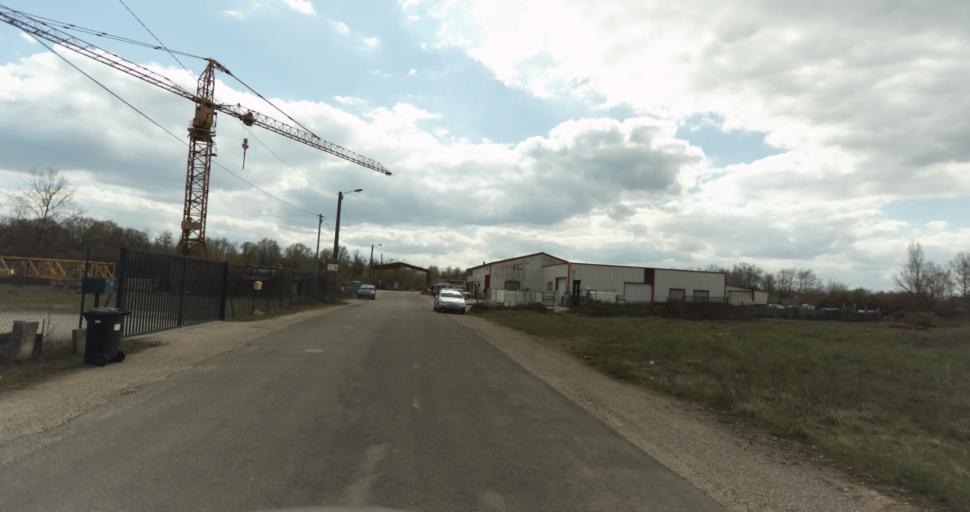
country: FR
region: Bourgogne
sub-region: Departement de la Cote-d'Or
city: Auxonne
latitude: 47.1951
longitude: 5.4169
